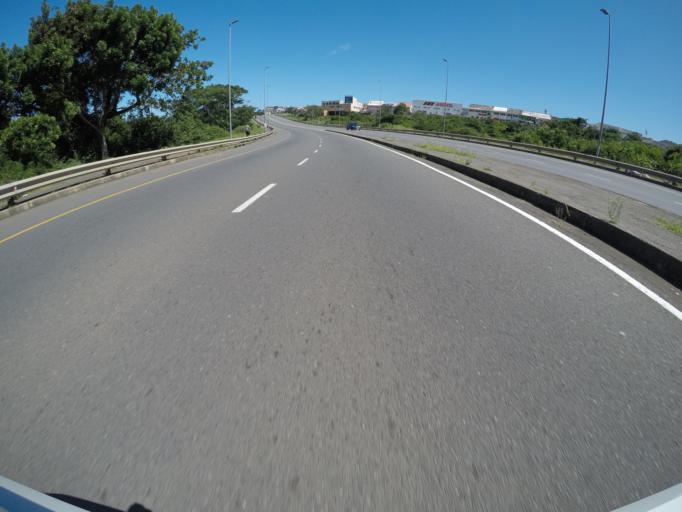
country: ZA
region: Eastern Cape
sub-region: Buffalo City Metropolitan Municipality
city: East London
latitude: -33.0043
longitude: 27.9128
